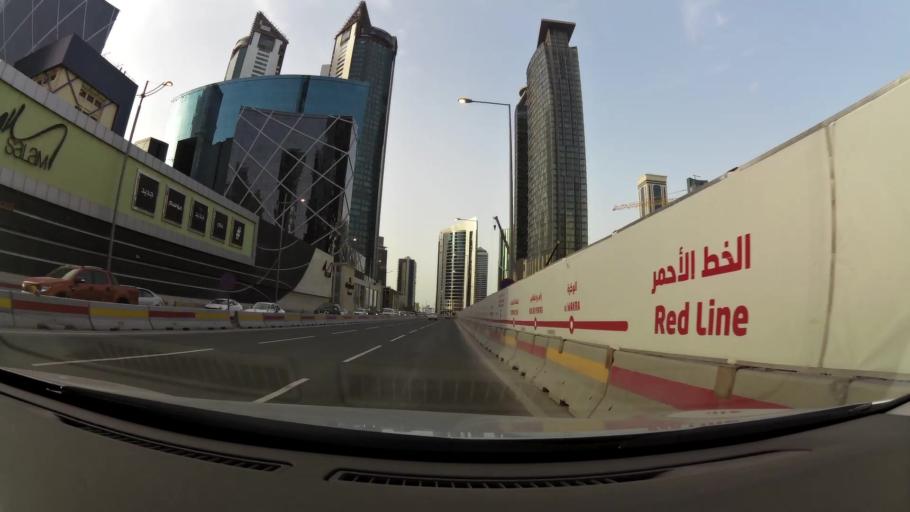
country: QA
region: Baladiyat ad Dawhah
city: Doha
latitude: 25.3222
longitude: 51.5275
